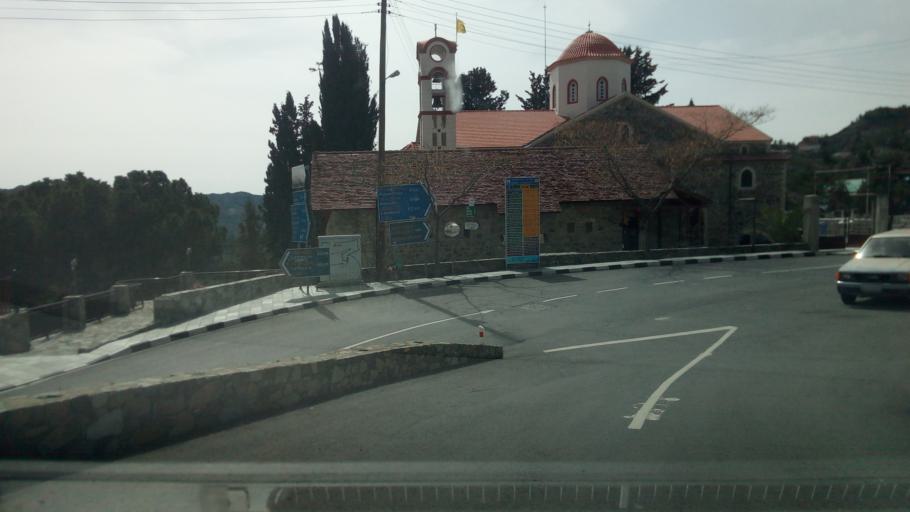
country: CY
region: Limassol
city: Kyperounta
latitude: 34.9173
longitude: 33.0178
